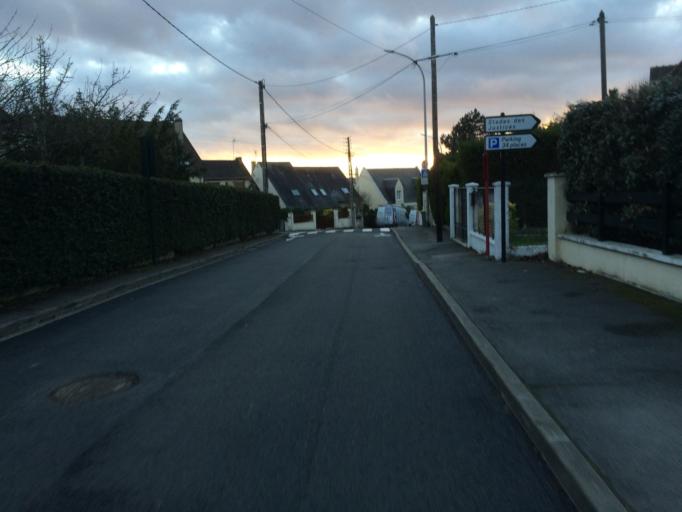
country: FR
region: Ile-de-France
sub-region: Departement de l'Essonne
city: Verrieres-le-Buisson
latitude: 48.7421
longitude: 2.2545
